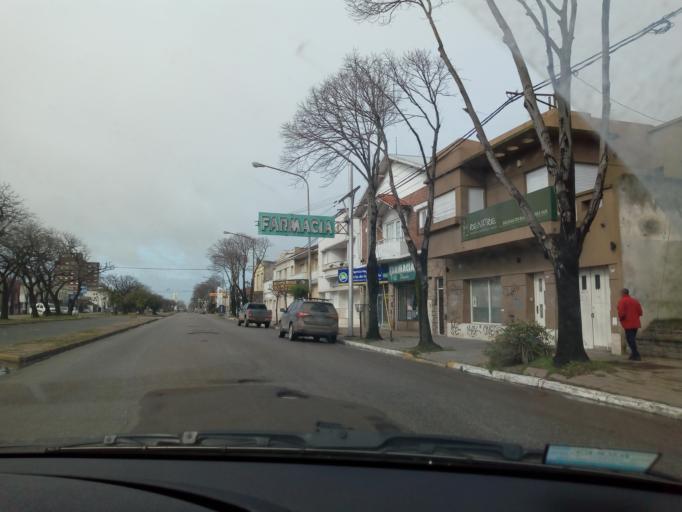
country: AR
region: Buenos Aires
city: Necochea
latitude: -38.5577
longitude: -58.7354
